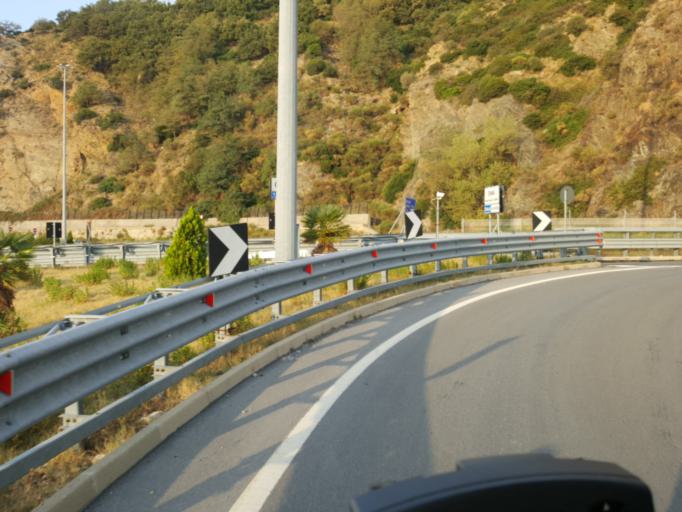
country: IT
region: Liguria
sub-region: Provincia di Savona
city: Bergeggi
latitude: 44.2548
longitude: 8.4514
